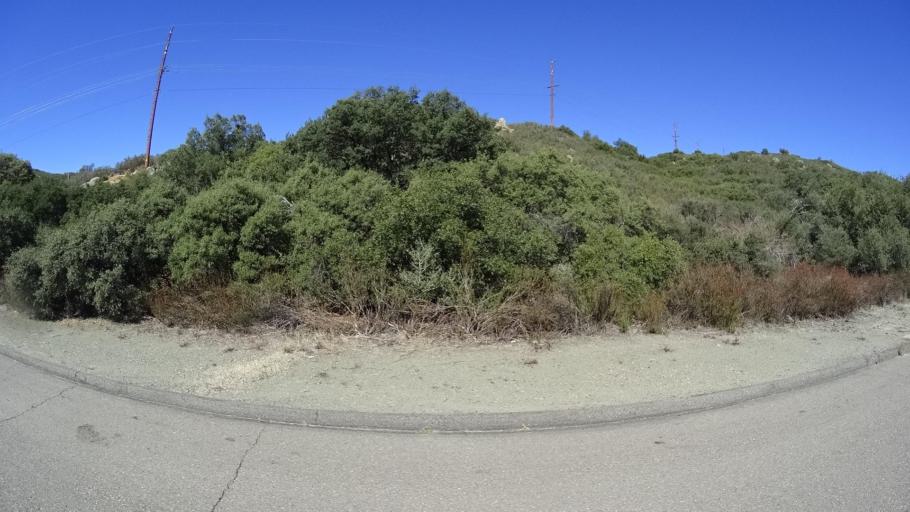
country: US
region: California
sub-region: San Diego County
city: Descanso
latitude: 32.8248
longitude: -116.6268
